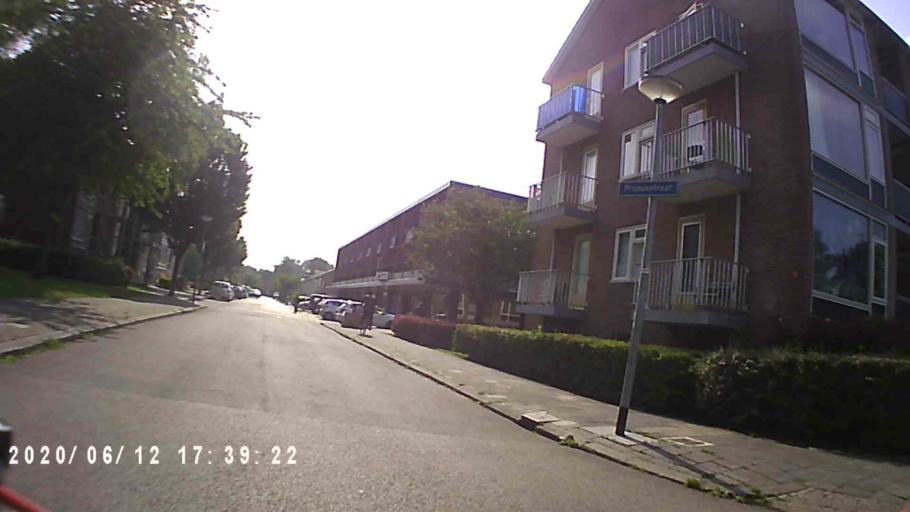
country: NL
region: Groningen
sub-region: Gemeente Groningen
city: Korrewegwijk
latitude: 53.2355
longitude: 6.5510
